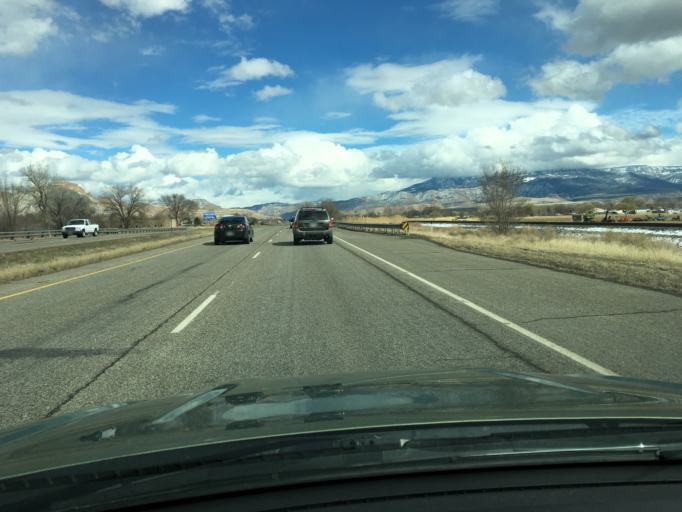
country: US
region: Colorado
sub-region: Mesa County
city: Fruitvale
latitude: 39.0793
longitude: -108.4870
